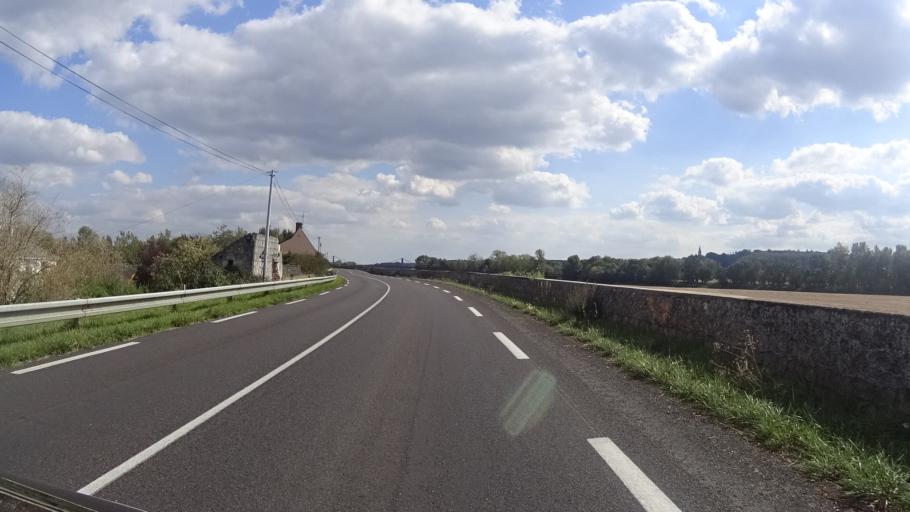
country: FR
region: Pays de la Loire
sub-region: Departement de Maine-et-Loire
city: Gennes
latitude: 47.3550
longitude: -0.2397
